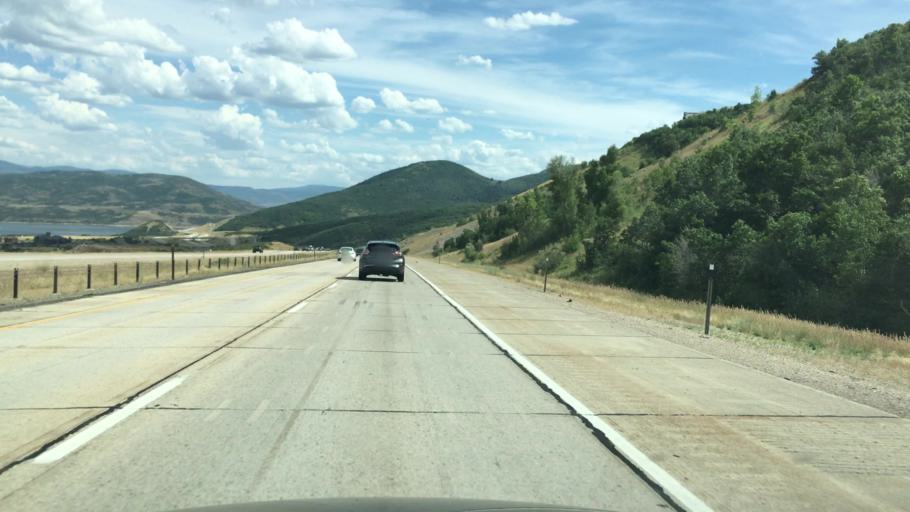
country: US
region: Utah
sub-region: Summit County
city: Park City
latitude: 40.6457
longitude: -111.4545
